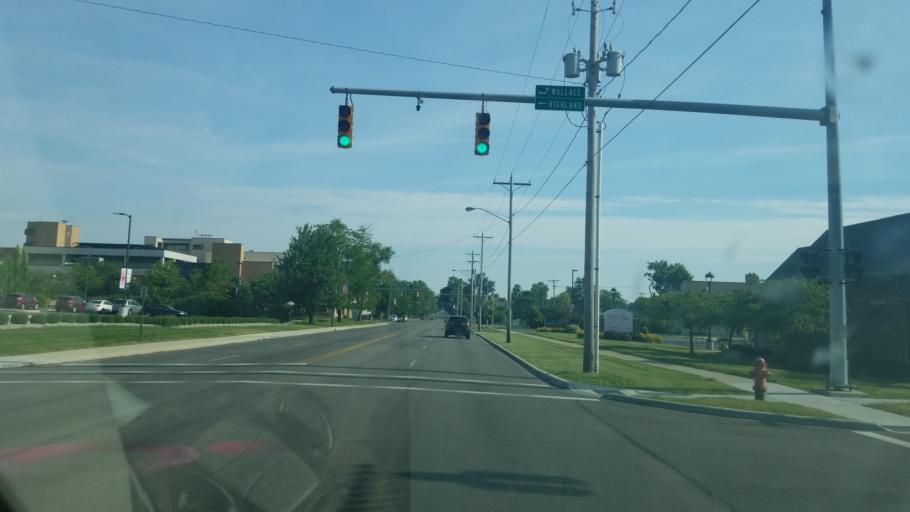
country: US
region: Ohio
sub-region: Hancock County
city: Findlay
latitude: 41.0159
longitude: -83.6503
